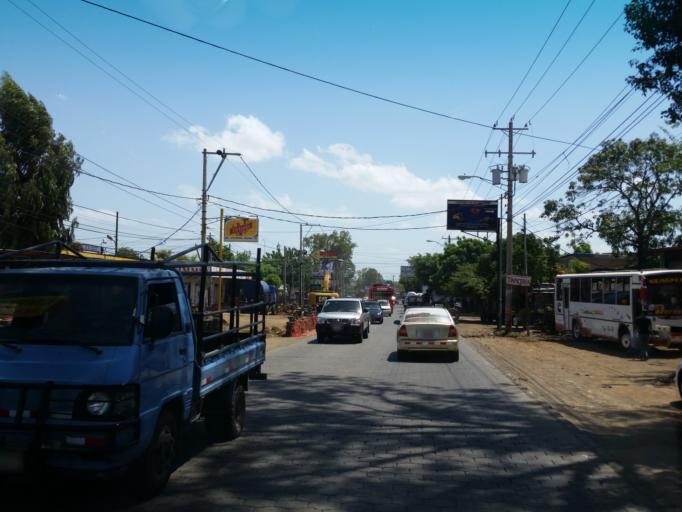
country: NI
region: Managua
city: Managua
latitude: 12.1366
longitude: -86.1974
